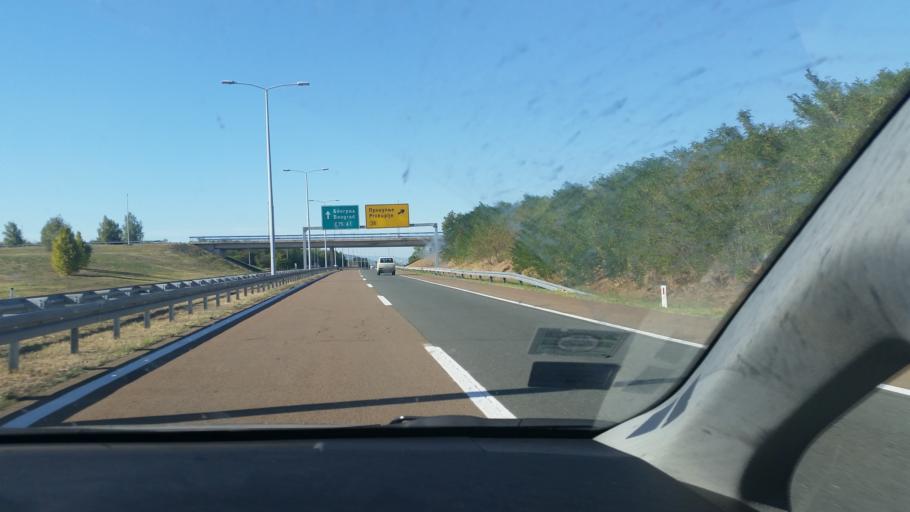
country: RS
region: Central Serbia
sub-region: Nisavski Okrug
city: Merosina
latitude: 43.2786
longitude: 21.8029
